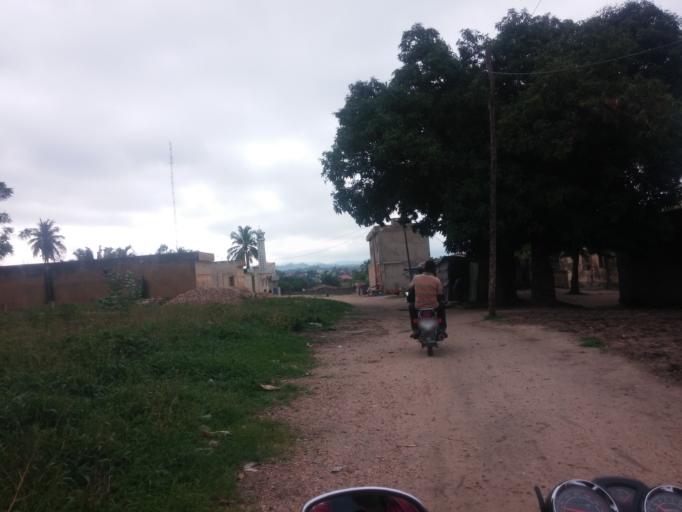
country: TG
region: Kara
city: Kara
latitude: 9.5448
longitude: 1.1821
